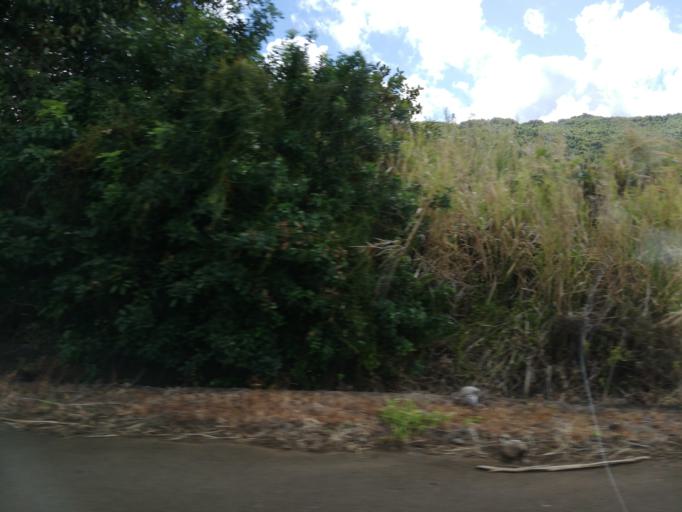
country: MU
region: Grand Port
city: Mahebourg
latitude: -20.3948
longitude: 57.6896
